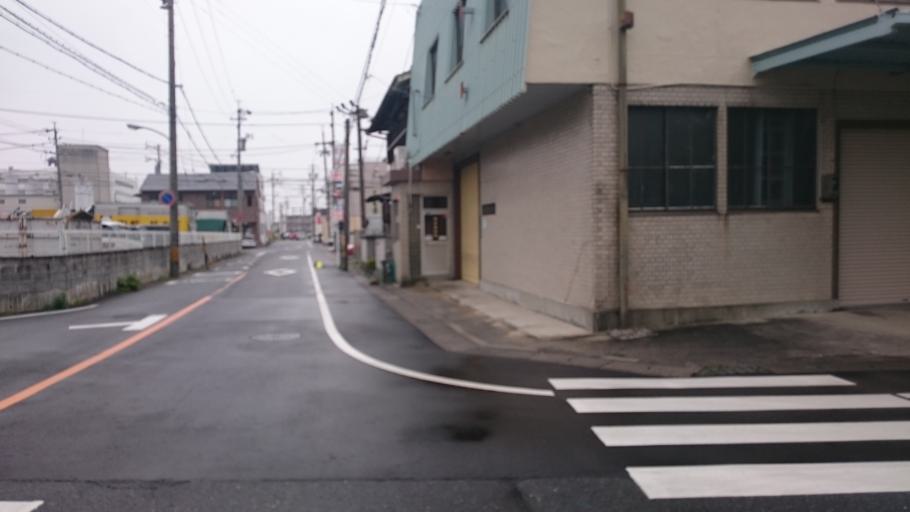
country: JP
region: Mie
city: Yokkaichi
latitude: 34.9599
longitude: 136.6260
